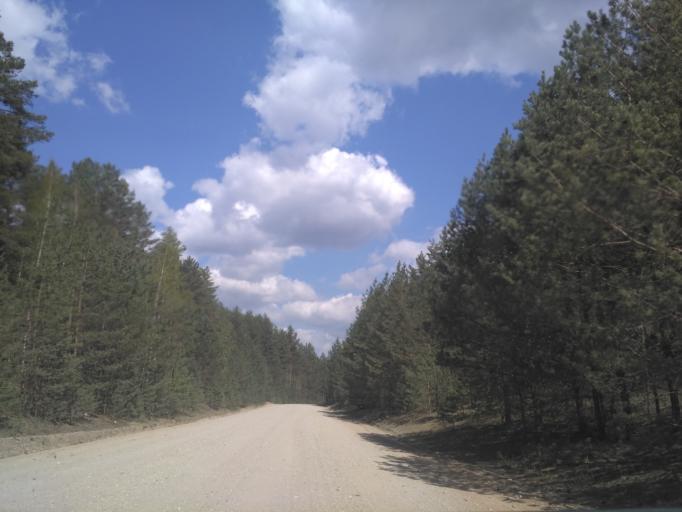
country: BY
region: Minsk
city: Radashkovichy
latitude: 54.2464
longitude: 27.2840
